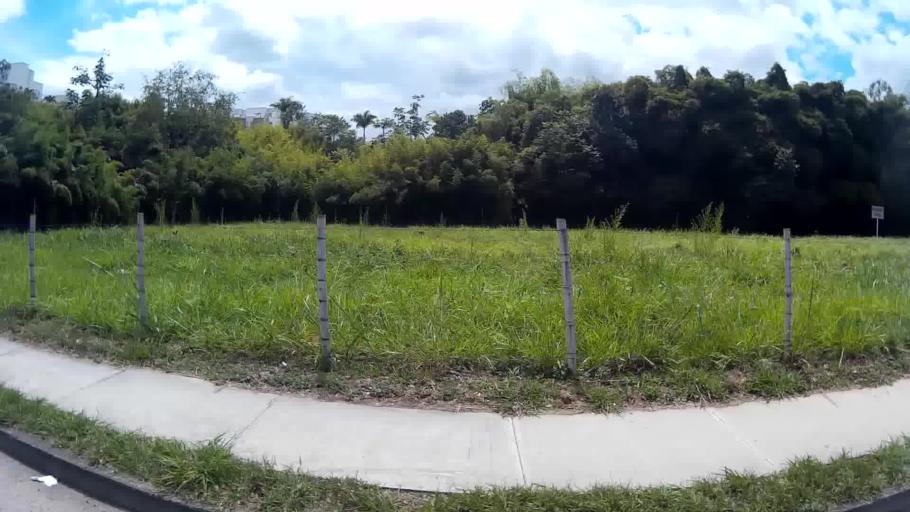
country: CO
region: Risaralda
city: Pereira
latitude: 4.8077
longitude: -75.7644
